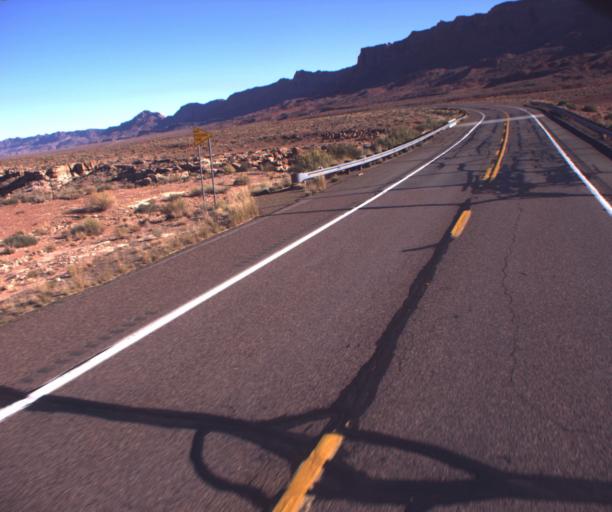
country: US
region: Arizona
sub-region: Coconino County
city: LeChee
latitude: 36.7200
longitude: -111.6449
